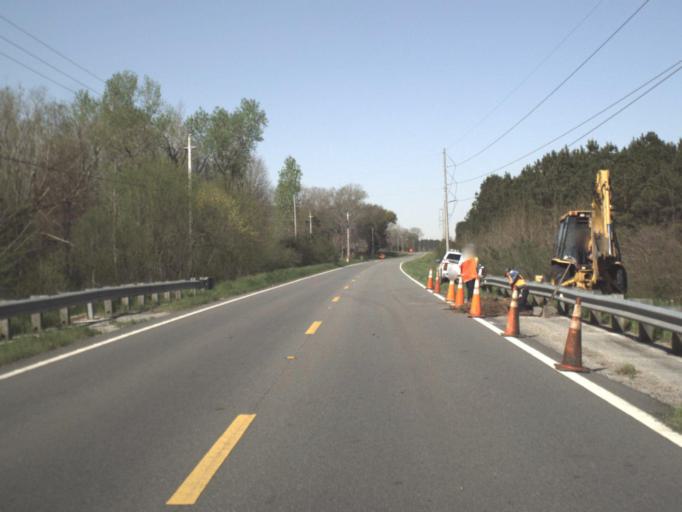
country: US
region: Florida
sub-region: Jackson County
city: Graceville
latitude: 30.9531
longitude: -85.4508
